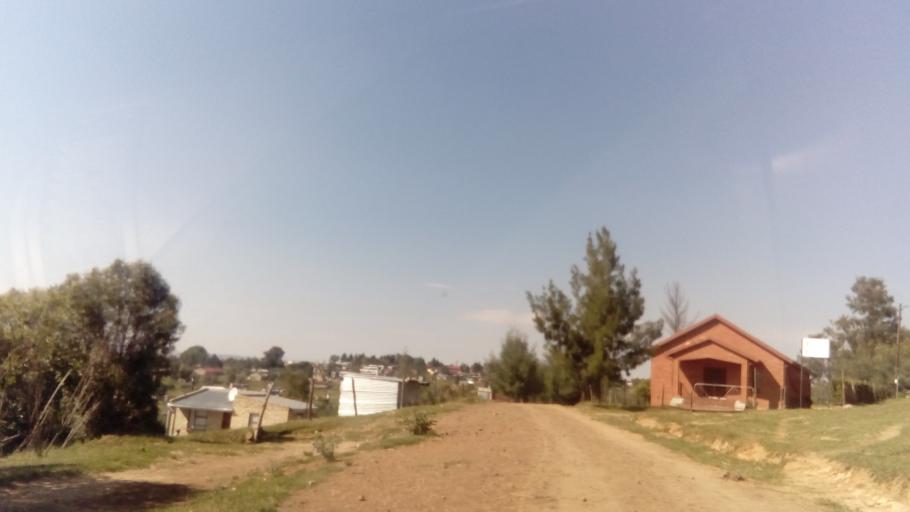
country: LS
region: Berea
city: Teyateyaneng
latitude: -29.1403
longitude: 27.7575
